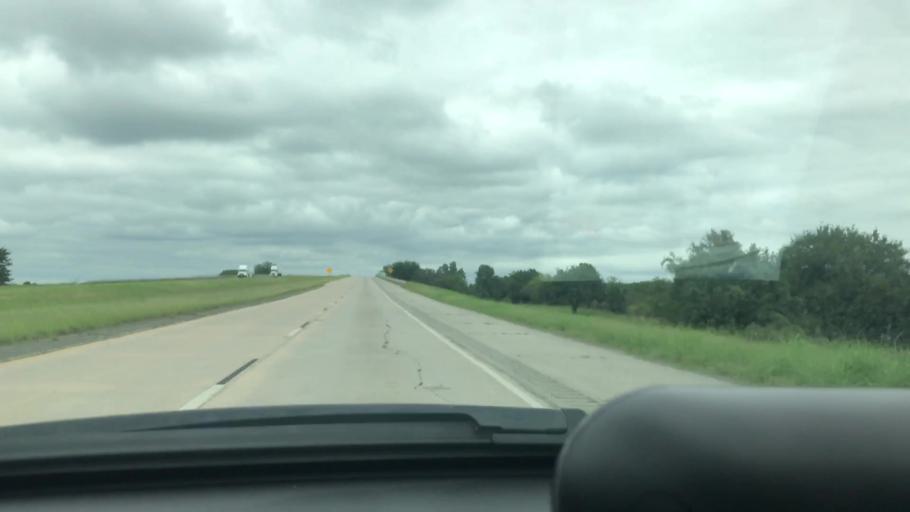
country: US
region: Oklahoma
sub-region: Wagoner County
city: Wagoner
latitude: 35.8794
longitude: -95.4033
